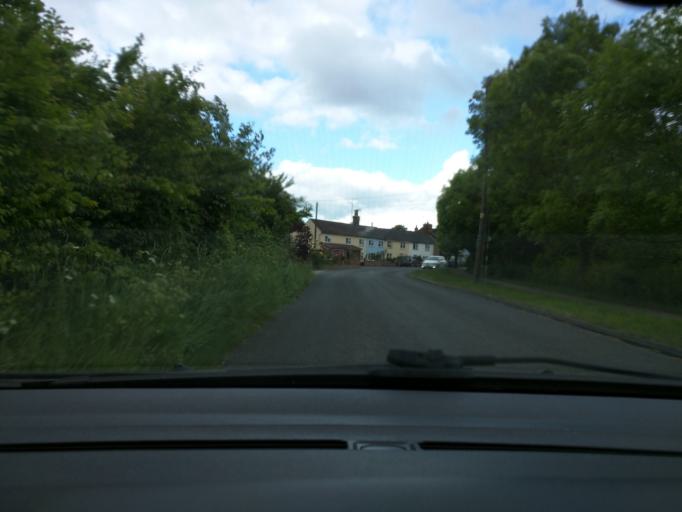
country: GB
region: England
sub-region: Suffolk
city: Saxmundham
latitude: 52.2271
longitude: 1.4871
